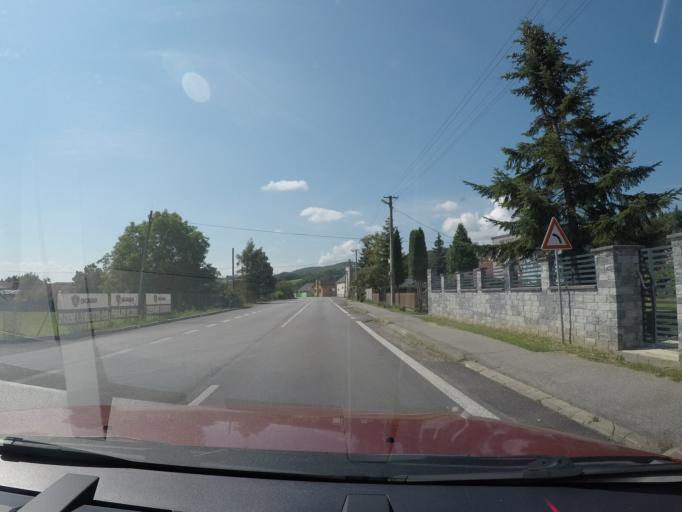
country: SK
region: Presovsky
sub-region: Okres Presov
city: Presov
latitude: 48.8780
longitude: 21.2462
